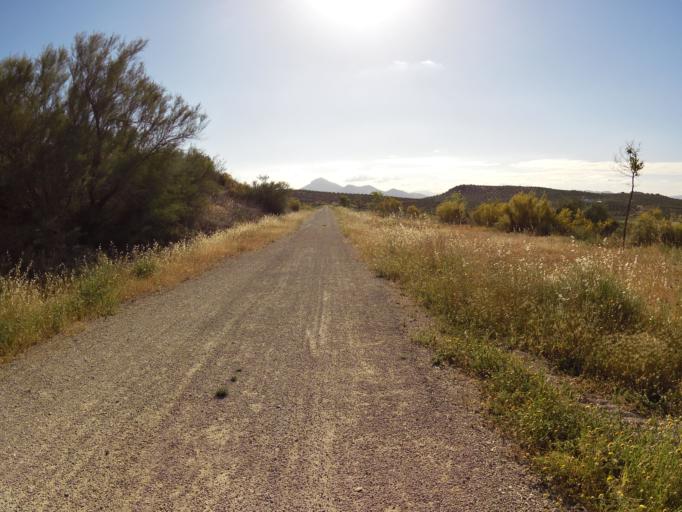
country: ES
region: Andalusia
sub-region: Province of Cordoba
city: Luque
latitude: 37.5830
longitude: -4.2066
